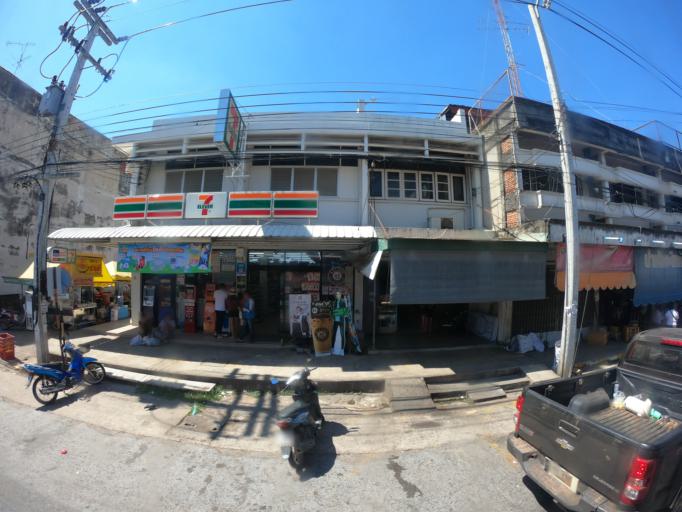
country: TH
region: Khon Kaen
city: Ban Phai
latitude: 16.0602
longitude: 102.7265
